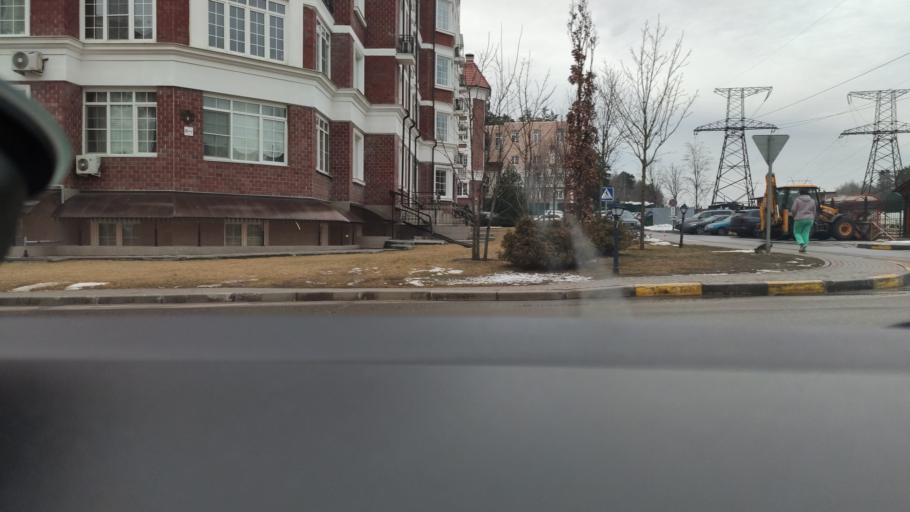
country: RU
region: Moscow
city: Zagor'ye
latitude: 55.5238
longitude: 37.6399
